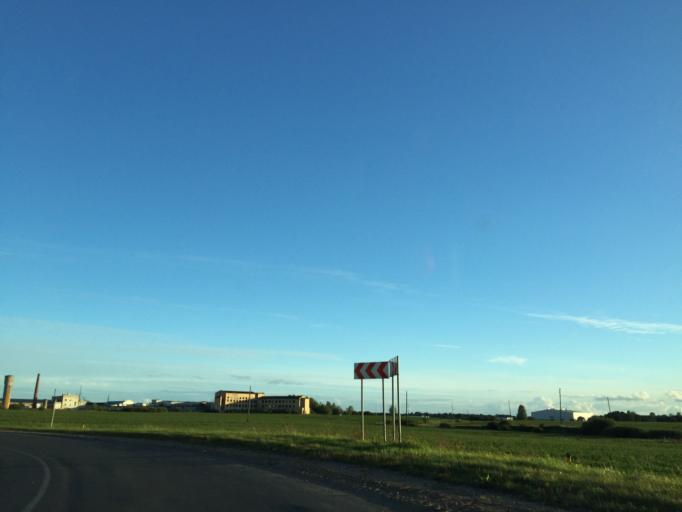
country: LV
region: Saldus Rajons
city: Saldus
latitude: 56.6877
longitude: 22.4584
